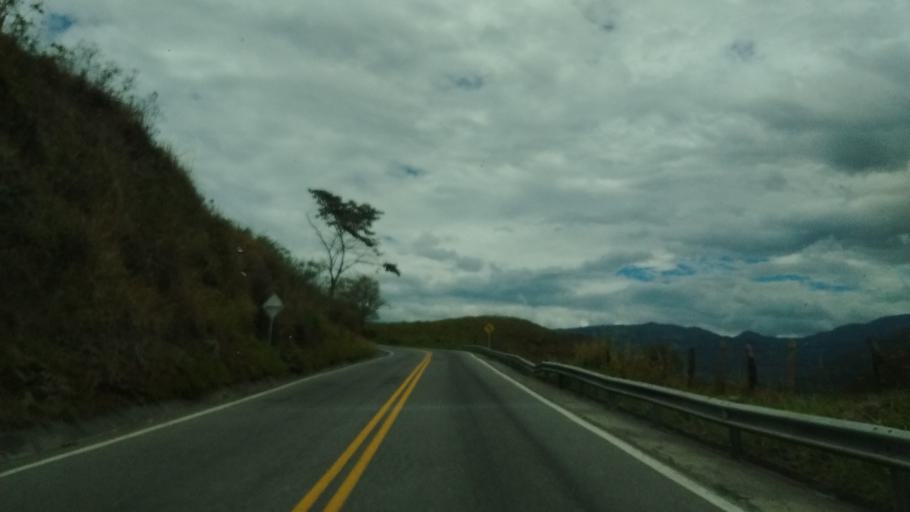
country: CO
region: Cauca
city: La Sierra
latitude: 2.2068
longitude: -76.8018
